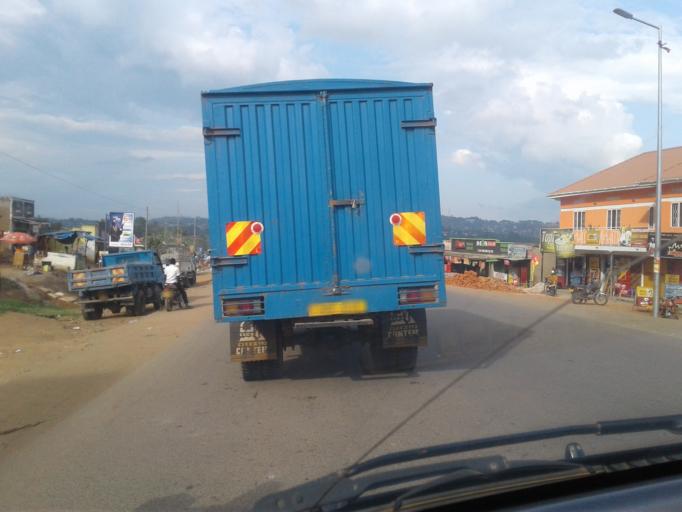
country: UG
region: Central Region
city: Masaka
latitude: -0.3396
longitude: 31.7063
